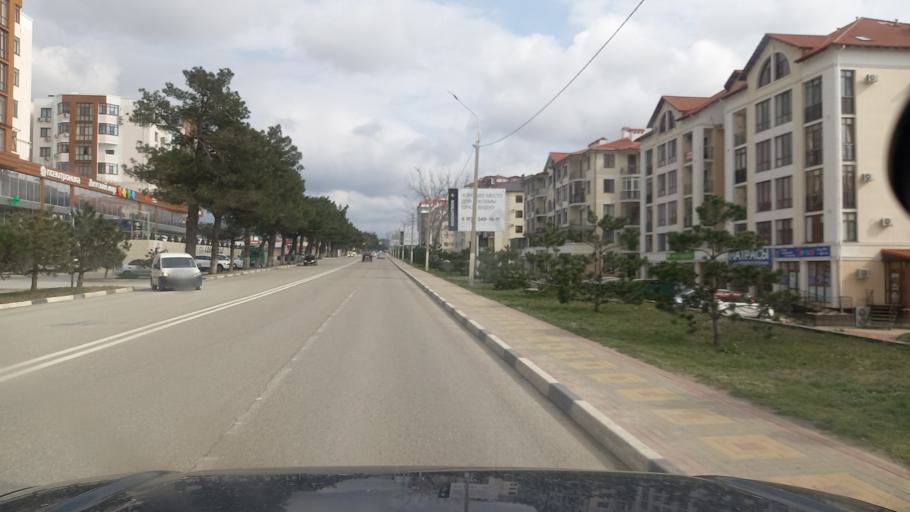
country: RU
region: Krasnodarskiy
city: Gelendzhik
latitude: 44.5602
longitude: 38.0951
